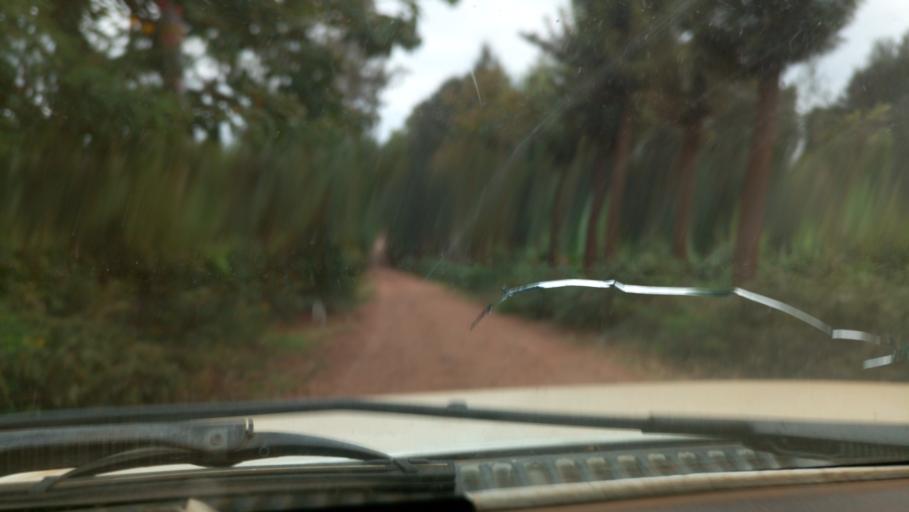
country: KE
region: Murang'a District
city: Maragua
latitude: -0.8941
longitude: 37.1937
